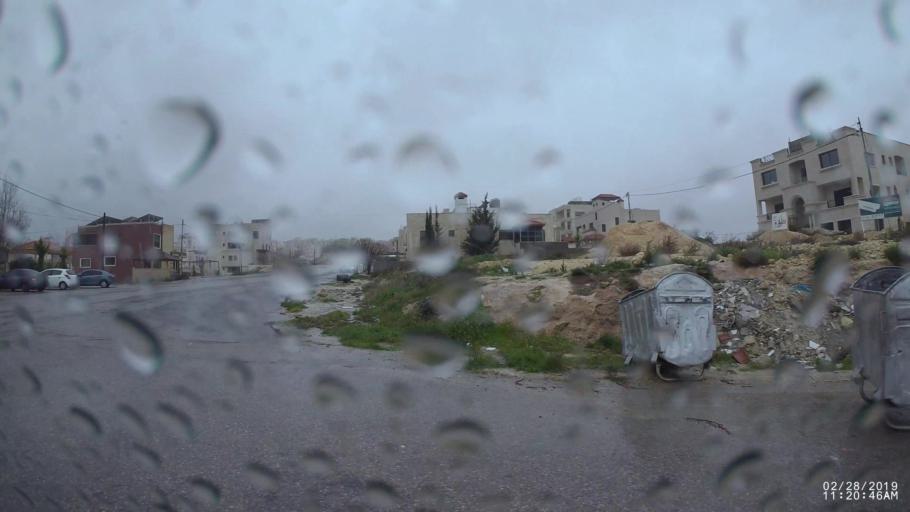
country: JO
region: Amman
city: Al Jubayhah
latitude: 32.0102
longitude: 35.9032
